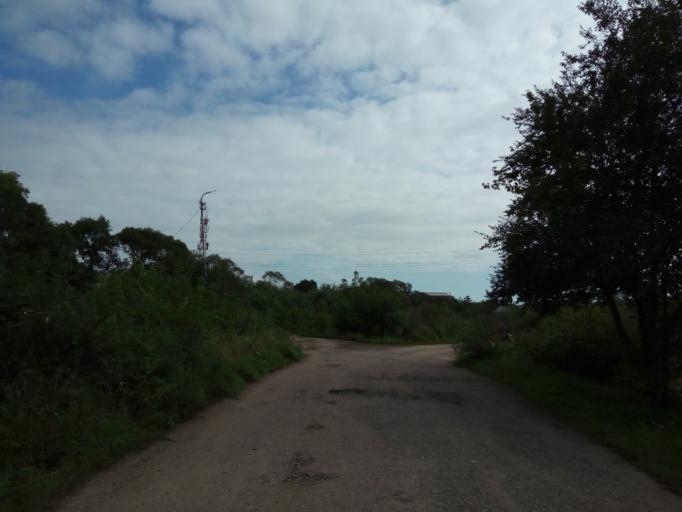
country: RU
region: Primorskiy
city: Dal'nerechensk
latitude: 45.9289
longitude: 133.7255
